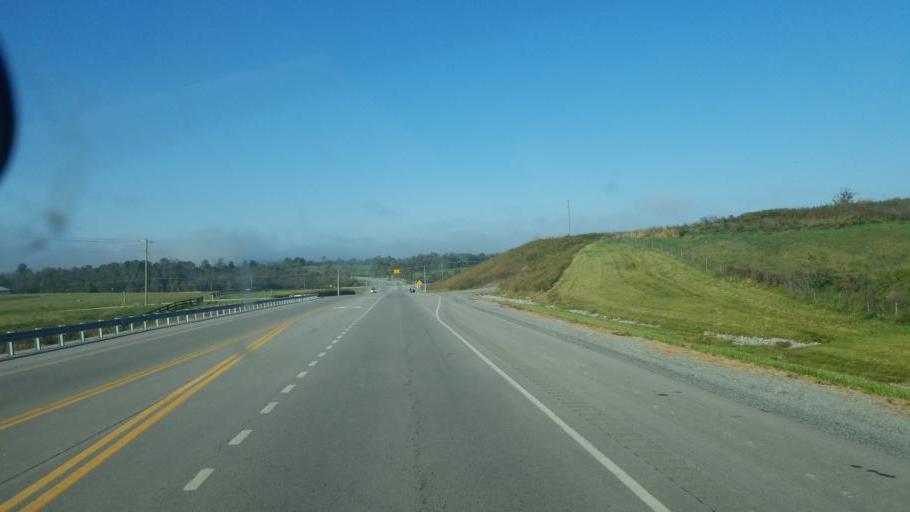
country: US
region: Kentucky
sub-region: Fleming County
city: Flemingsburg
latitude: 38.4415
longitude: -83.7367
